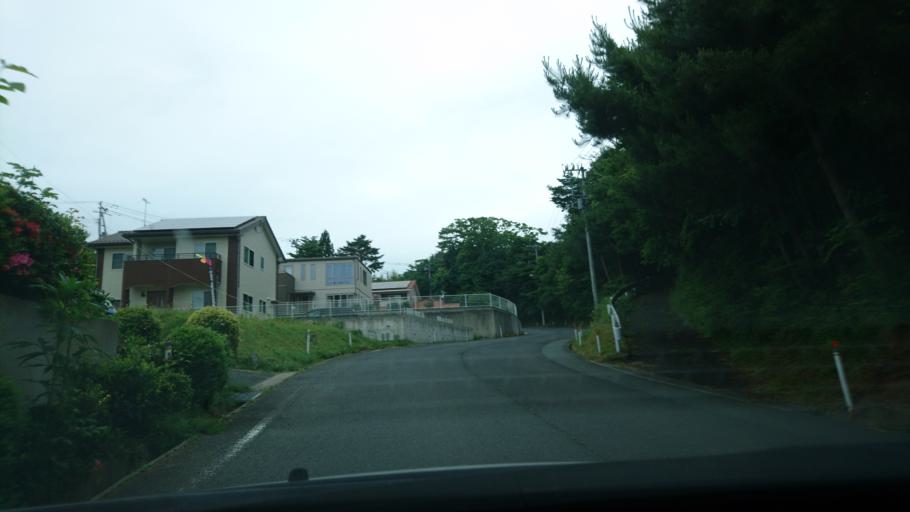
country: JP
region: Miyagi
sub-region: Oshika Gun
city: Onagawa Cho
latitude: 38.7780
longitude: 141.5130
